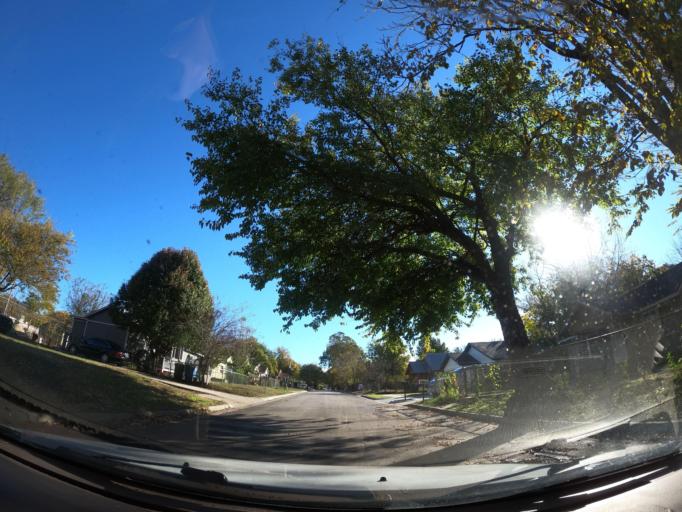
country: US
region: Oklahoma
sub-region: Tulsa County
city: Tulsa
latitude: 36.1761
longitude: -95.9644
